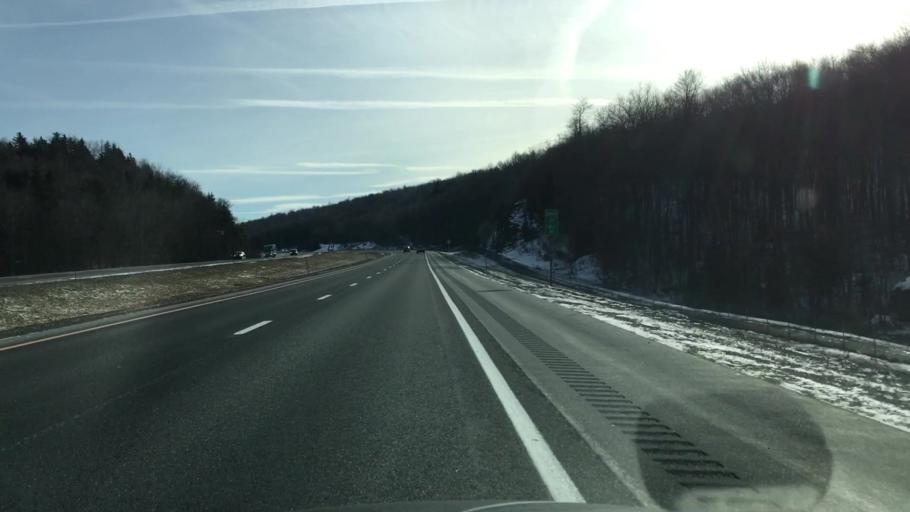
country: US
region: New Hampshire
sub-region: Grafton County
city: Enfield
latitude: 43.5788
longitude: -72.1615
